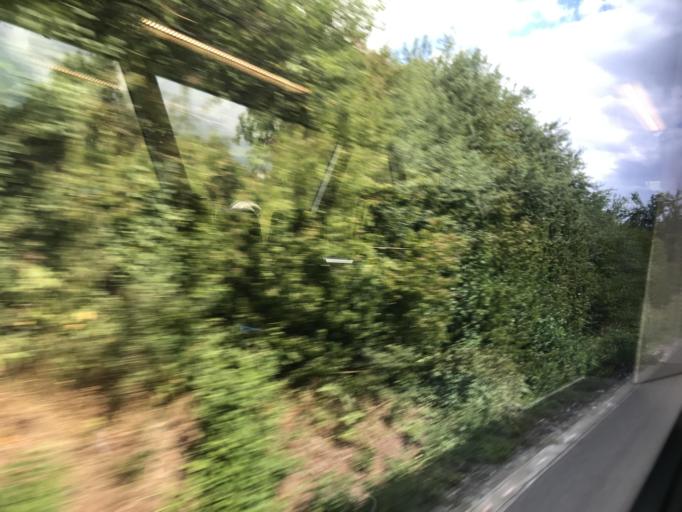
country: DE
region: Bavaria
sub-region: Regierungsbezirk Unterfranken
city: Hammelburg
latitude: 50.1288
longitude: 9.8423
